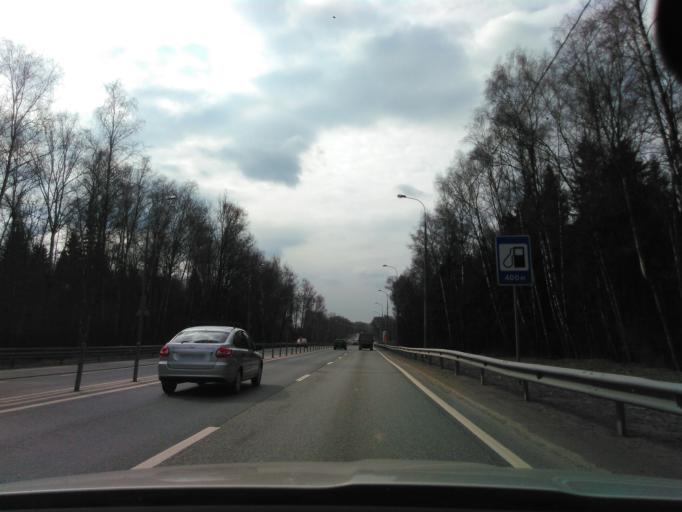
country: RU
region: Moskovskaya
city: Marfino
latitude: 56.0231
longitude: 37.5441
